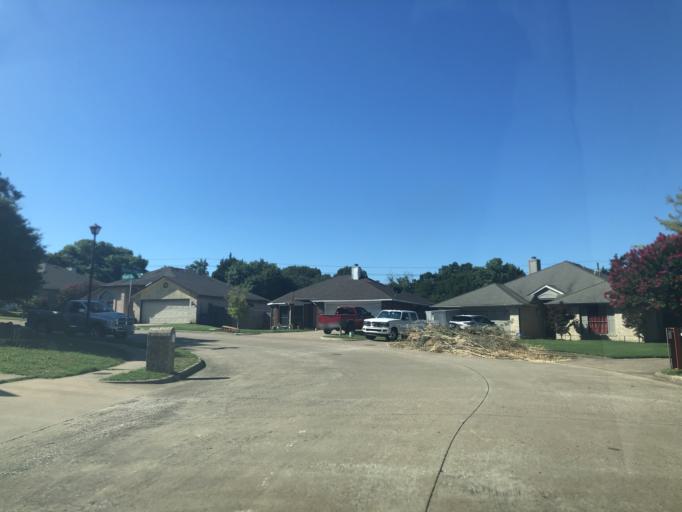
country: US
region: Texas
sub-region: Dallas County
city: Duncanville
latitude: 32.6641
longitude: -96.9365
